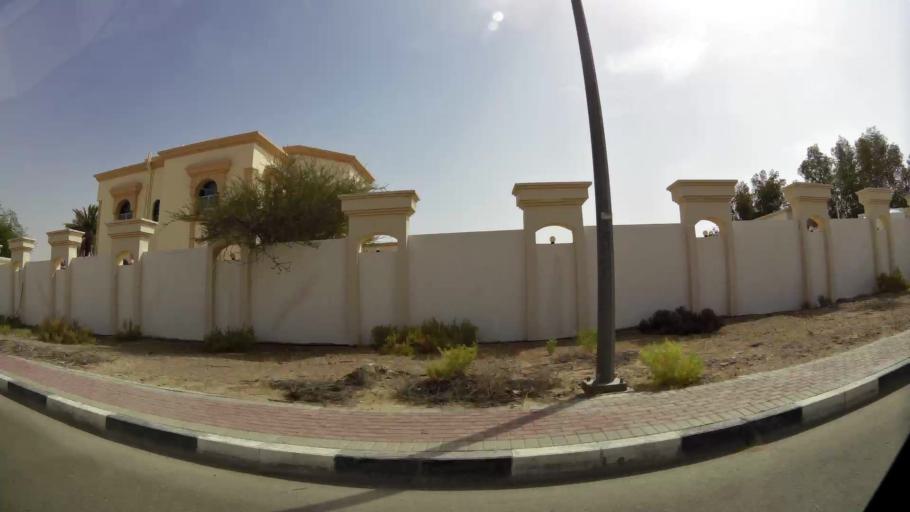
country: AE
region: Abu Dhabi
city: Al Ain
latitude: 24.1674
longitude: 55.7005
